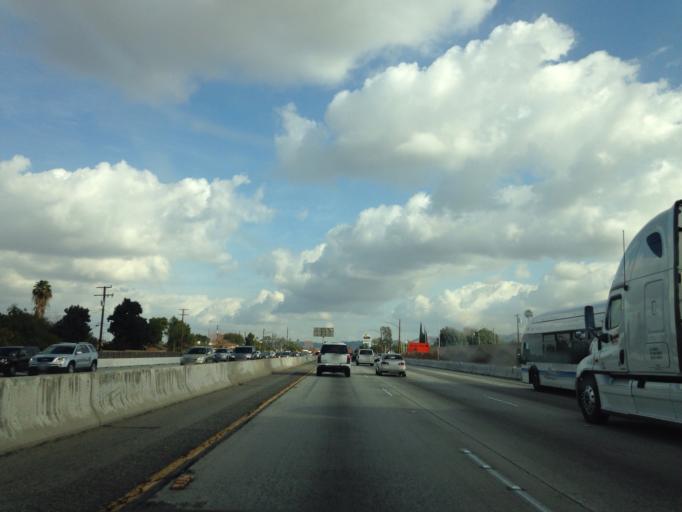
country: US
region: California
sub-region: Los Angeles County
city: West Covina
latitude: 34.0722
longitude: -117.9147
